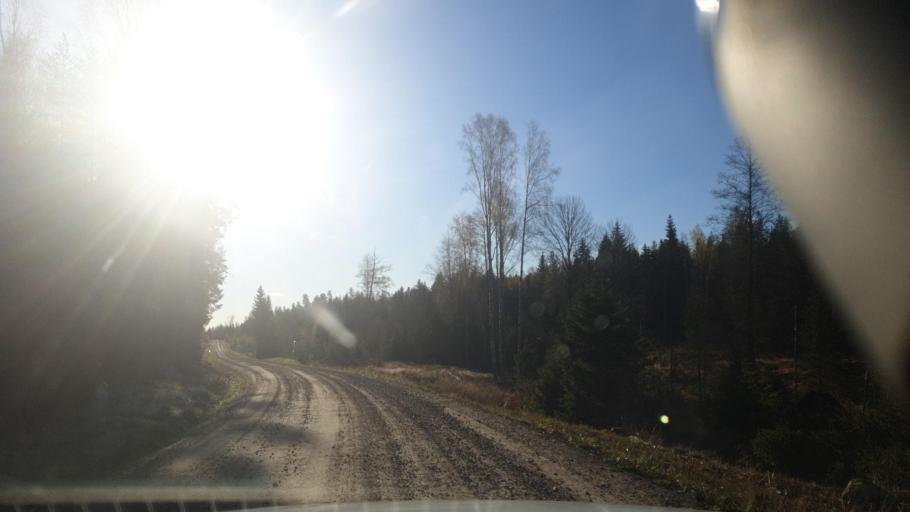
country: SE
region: Vaermland
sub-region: Karlstads Kommun
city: Edsvalla
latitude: 59.5243
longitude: 13.0015
